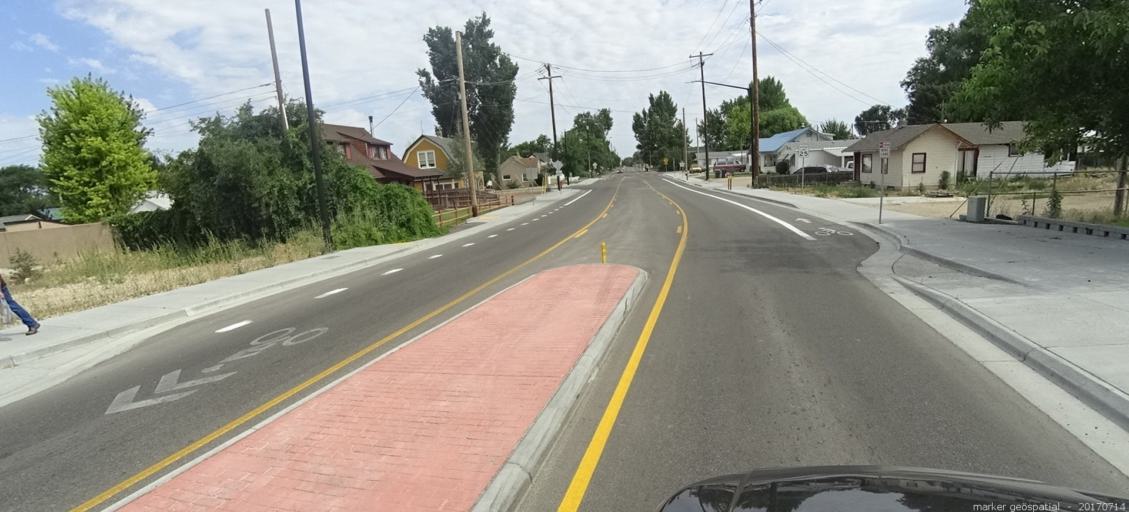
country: US
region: Idaho
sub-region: Ada County
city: Kuna
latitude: 43.4909
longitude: -116.4138
